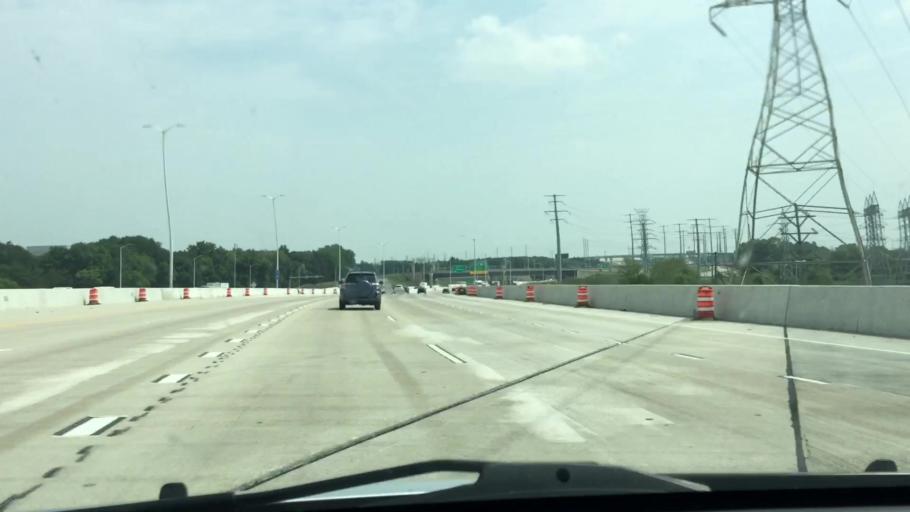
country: US
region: Wisconsin
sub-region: Waukesha County
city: Elm Grove
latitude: 43.0308
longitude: -88.0568
